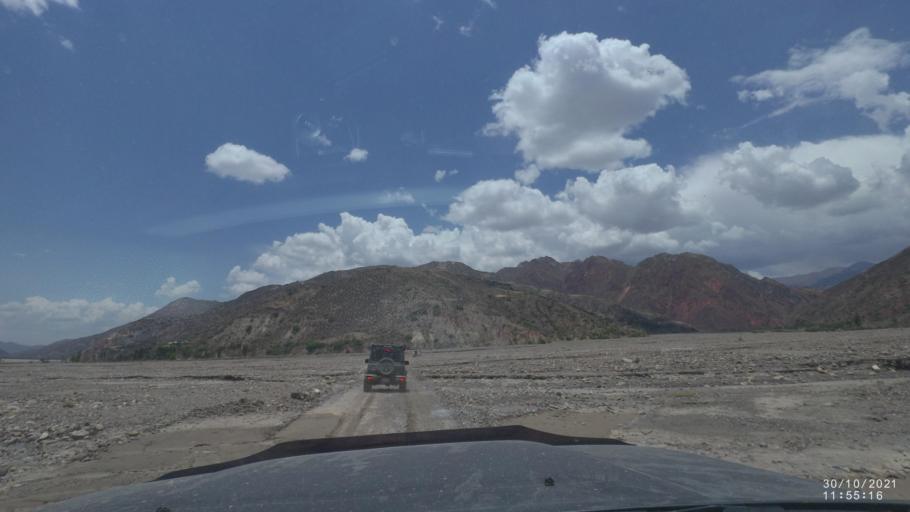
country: BO
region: Cochabamba
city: Colchani
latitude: -17.5198
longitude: -66.6197
